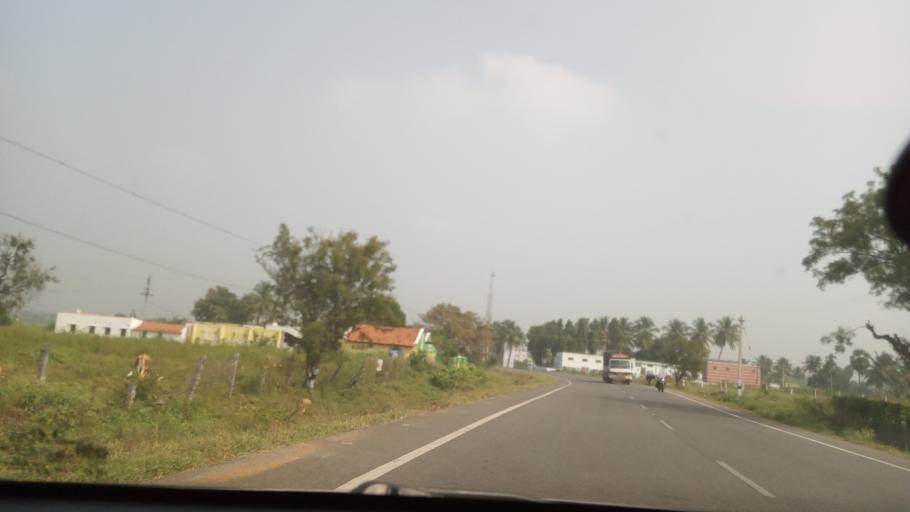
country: IN
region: Tamil Nadu
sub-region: Erode
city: Punjai Puliyampatti
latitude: 11.3772
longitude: 77.1722
